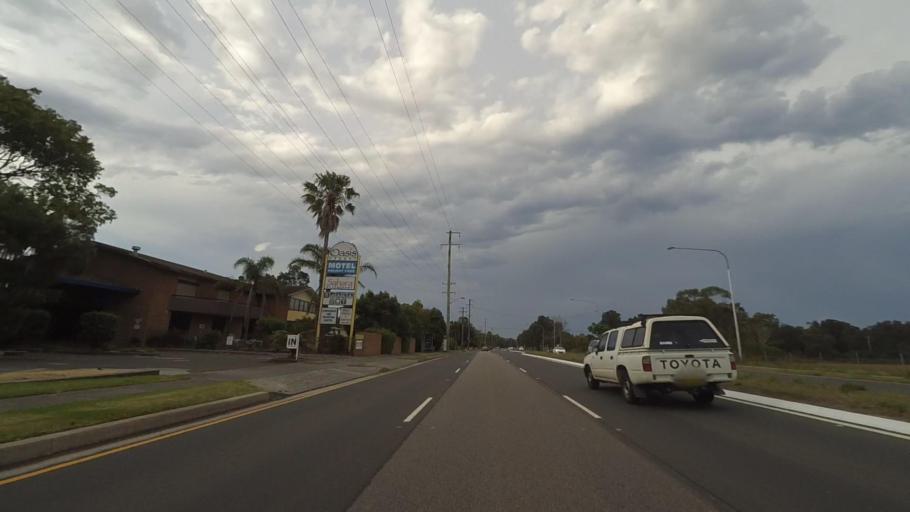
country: AU
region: New South Wales
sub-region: Wollongong
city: Lake Heights
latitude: -34.5181
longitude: 150.8722
